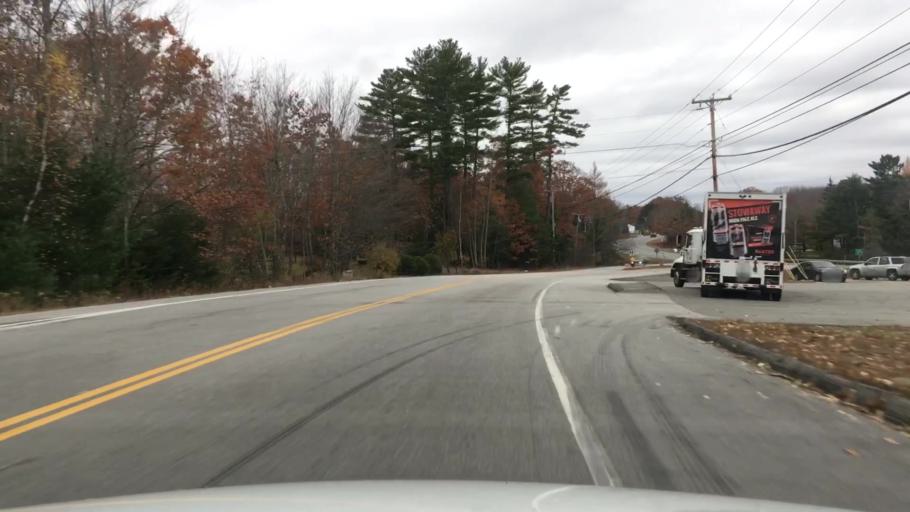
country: US
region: Maine
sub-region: Hancock County
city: Orland
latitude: 44.5593
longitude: -68.7082
